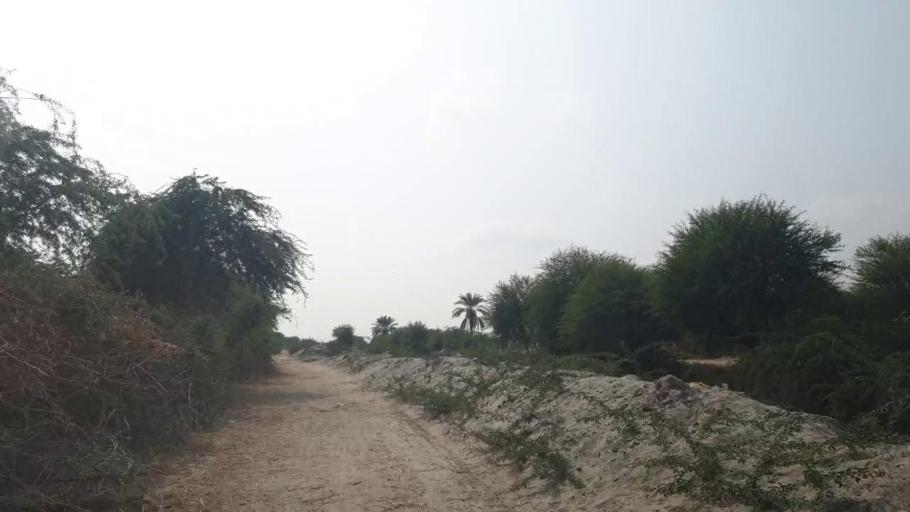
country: PK
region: Sindh
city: Badin
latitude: 24.6031
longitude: 68.7193
